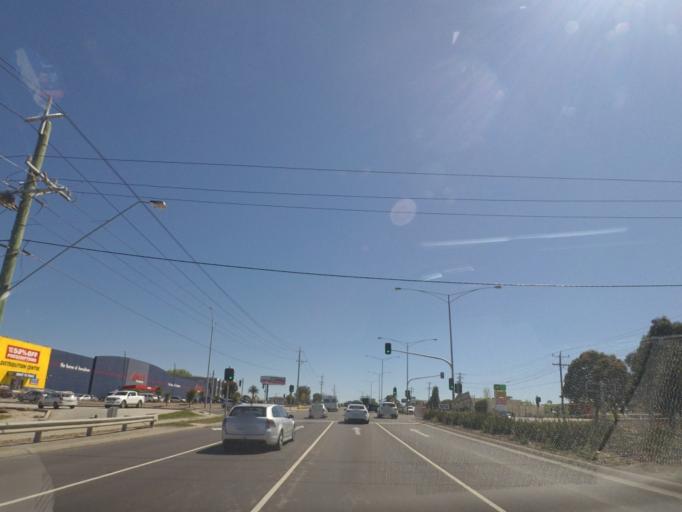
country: AU
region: Victoria
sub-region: Hume
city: Campbellfield
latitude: -37.6873
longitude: 144.9577
